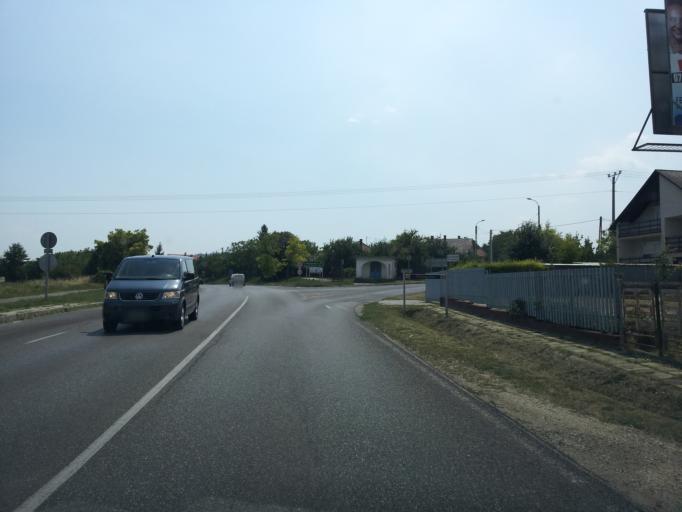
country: HU
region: Veszprem
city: Balatonalmadi
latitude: 47.0476
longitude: 18.0143
